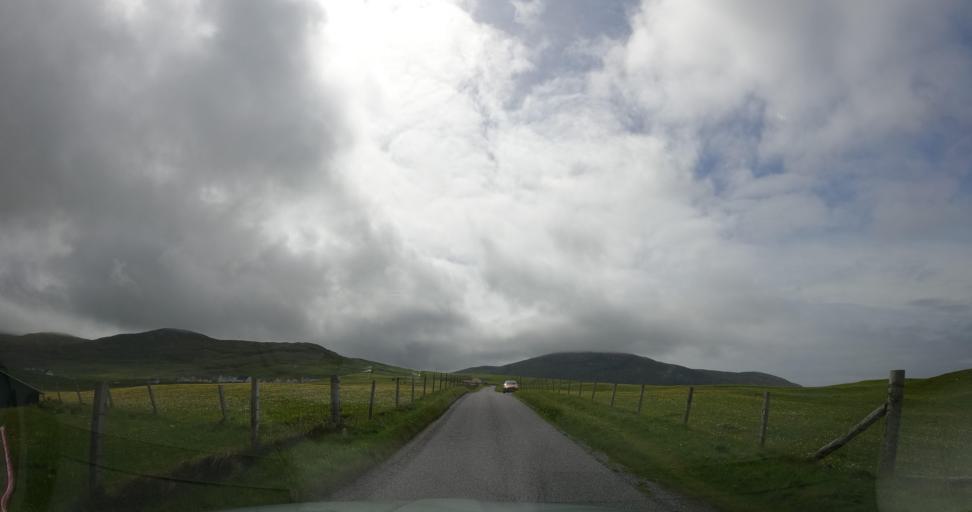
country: GB
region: Scotland
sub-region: Eilean Siar
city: Barra
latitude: 56.9851
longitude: -7.5093
